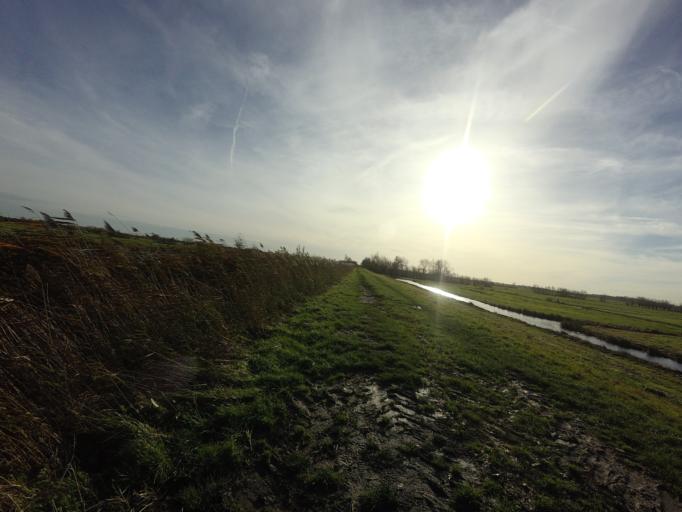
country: NL
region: South Holland
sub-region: Gemeente Vlist
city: Haastrecht
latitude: 52.0434
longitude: 4.7809
